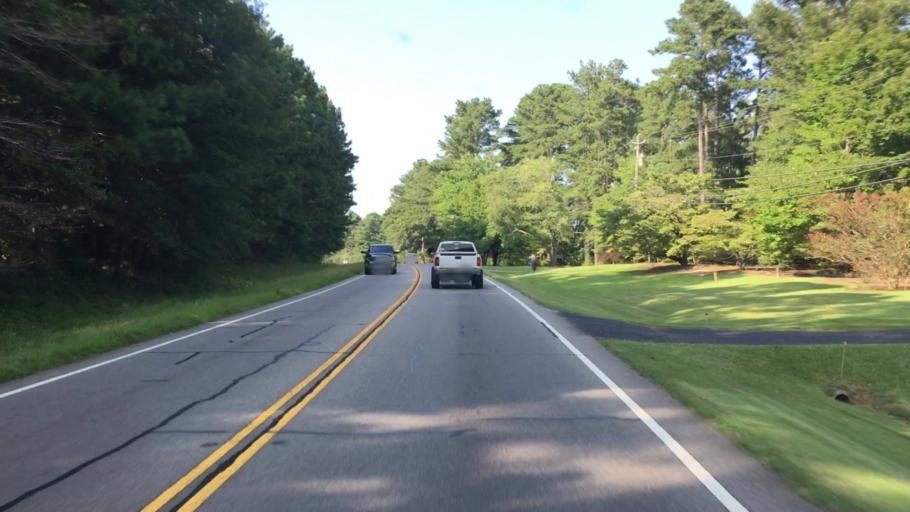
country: US
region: Georgia
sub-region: Barrow County
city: Russell
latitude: 33.9723
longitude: -83.7141
